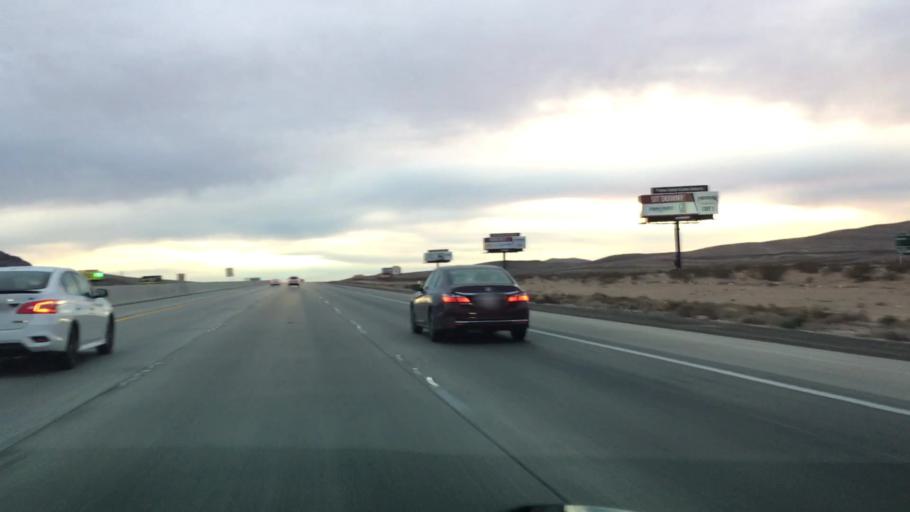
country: US
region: Nevada
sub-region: Clark County
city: Enterprise
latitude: 35.9232
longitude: -115.2004
